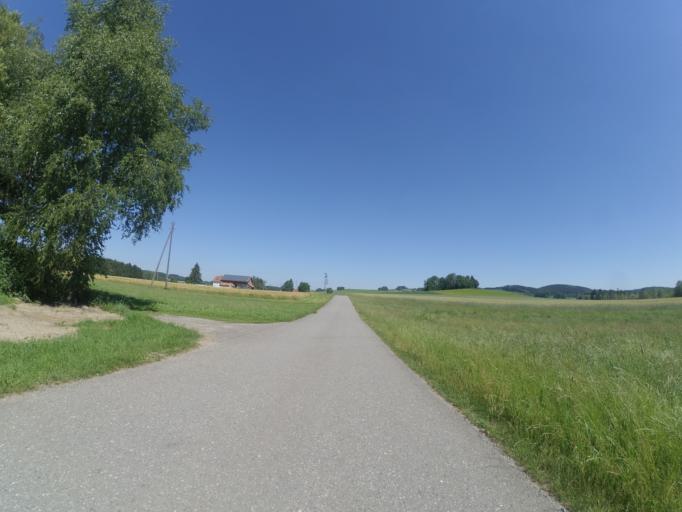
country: DE
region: Baden-Wuerttemberg
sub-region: Tuebingen Region
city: Bad Wurzach
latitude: 47.8784
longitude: 9.9199
